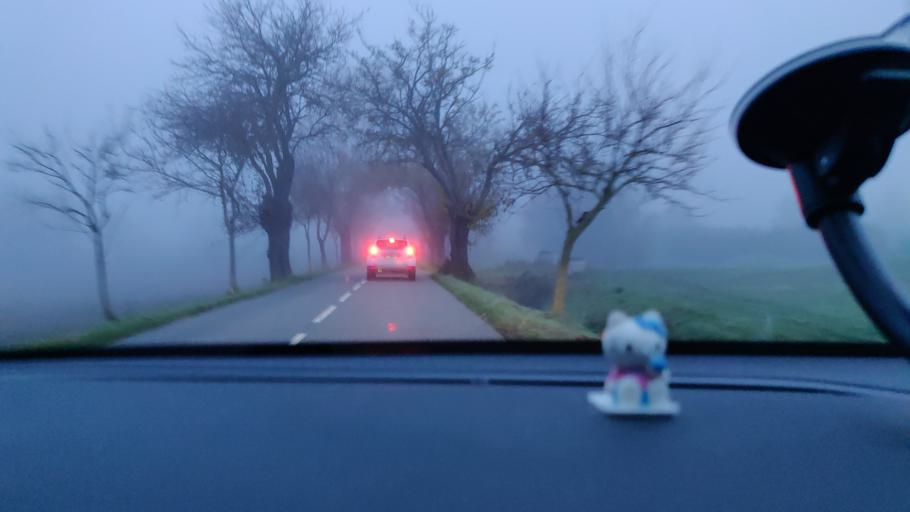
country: FR
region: Midi-Pyrenees
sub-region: Departement de la Haute-Garonne
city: Vieille-Toulouse
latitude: 43.4834
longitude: 1.4532
